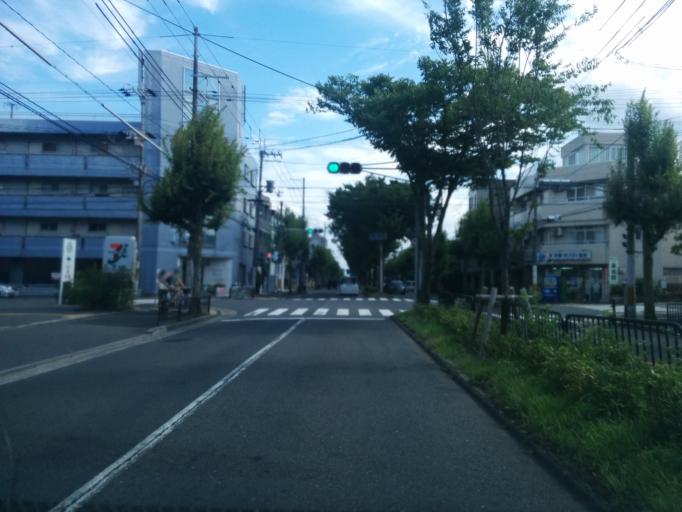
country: JP
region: Kyoto
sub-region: Kyoto-shi
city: Kamigyo-ku
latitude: 35.0531
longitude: 135.7515
